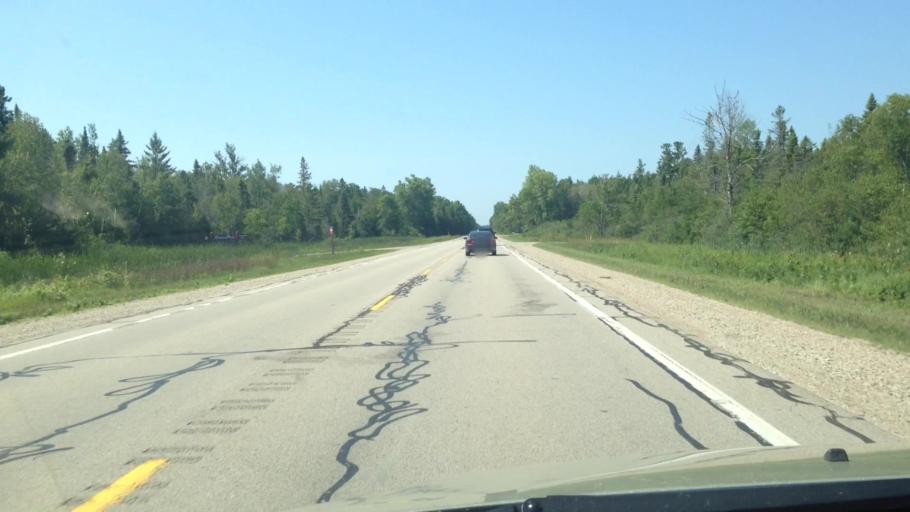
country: US
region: Michigan
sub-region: Menominee County
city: Menominee
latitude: 45.3540
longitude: -87.4033
